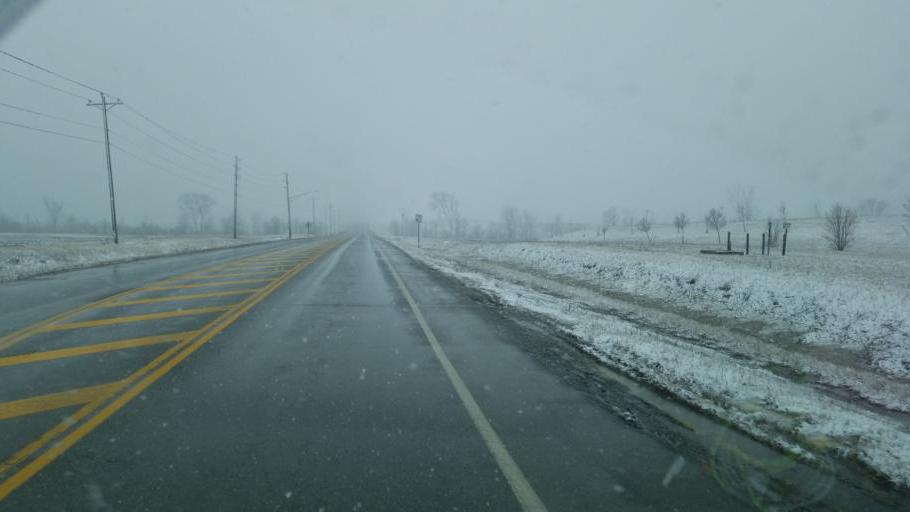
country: US
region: Ohio
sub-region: Champaign County
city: North Lewisburg
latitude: 40.3012
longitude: -83.5119
